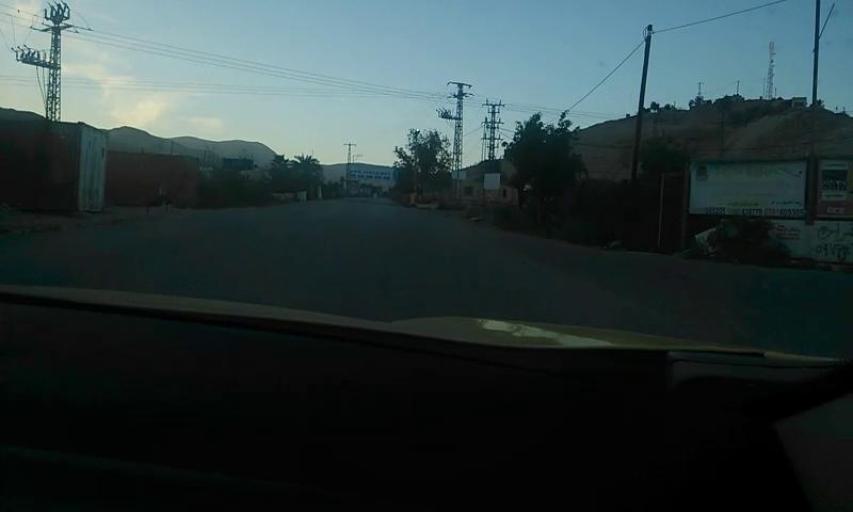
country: PS
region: West Bank
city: An Nuway`imah
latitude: 31.8943
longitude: 35.4289
